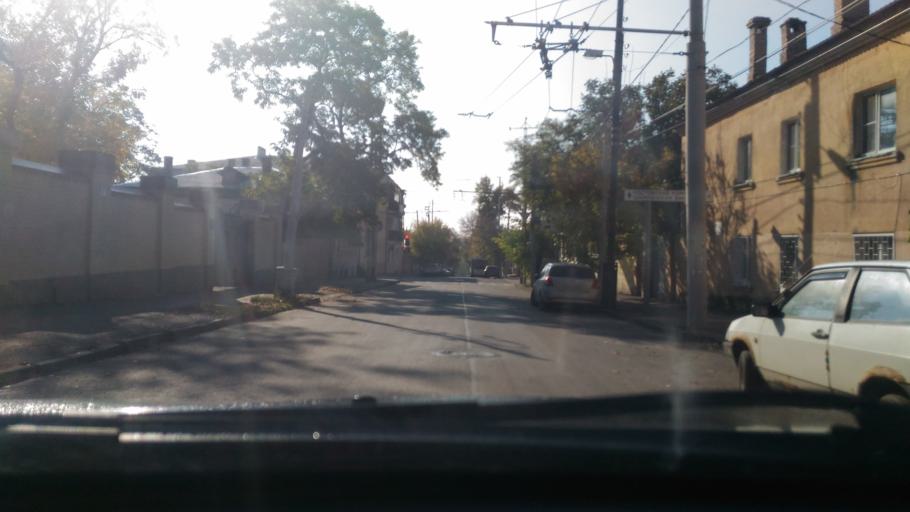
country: RU
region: Rostov
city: Rostov-na-Donu
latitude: 47.2280
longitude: 39.7632
